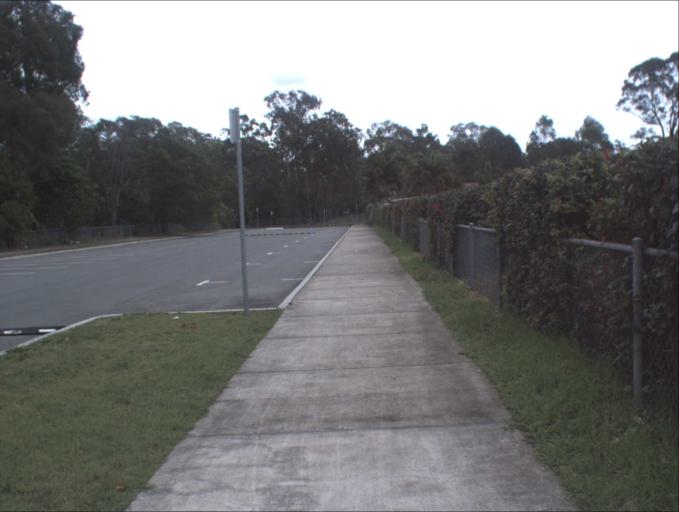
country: AU
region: Queensland
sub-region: Logan
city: Park Ridge South
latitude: -27.6854
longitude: 153.0229
